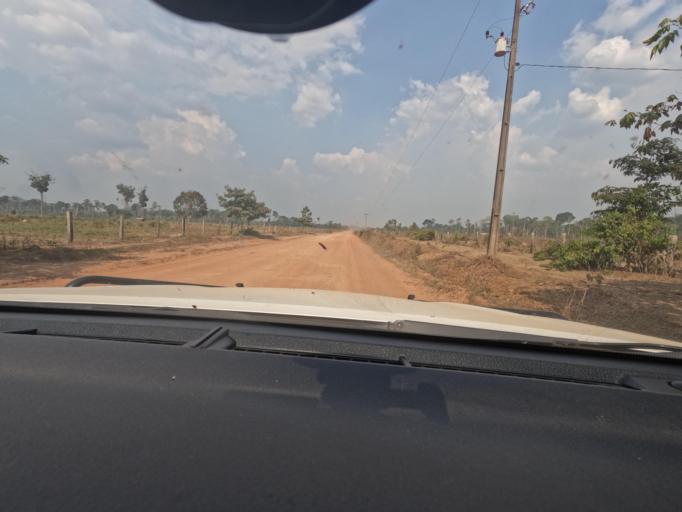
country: BR
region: Rondonia
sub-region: Porto Velho
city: Porto Velho
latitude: -8.6832
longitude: -63.2015
